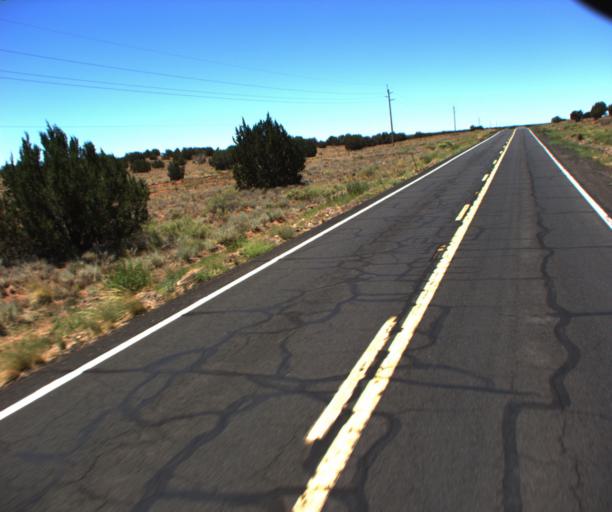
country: US
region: Arizona
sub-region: Coconino County
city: LeChee
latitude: 34.8534
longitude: -110.9242
